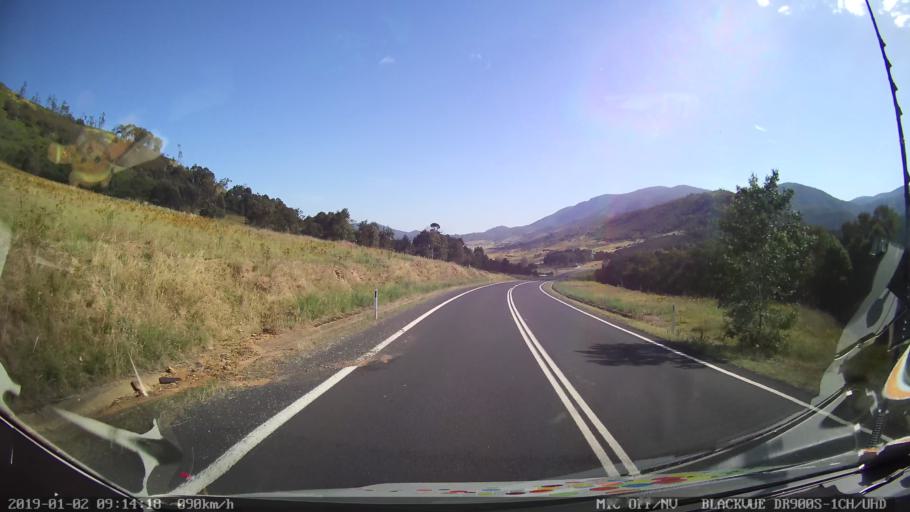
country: AU
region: New South Wales
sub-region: Tumut Shire
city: Tumut
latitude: -35.4790
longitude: 148.2731
